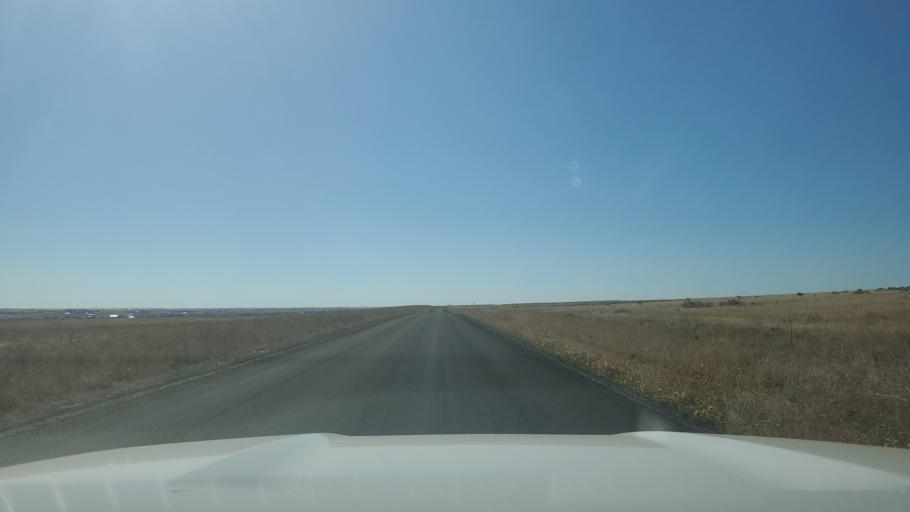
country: US
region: Colorado
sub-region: Adams County
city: Bennett
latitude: 39.7625
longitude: -104.3769
